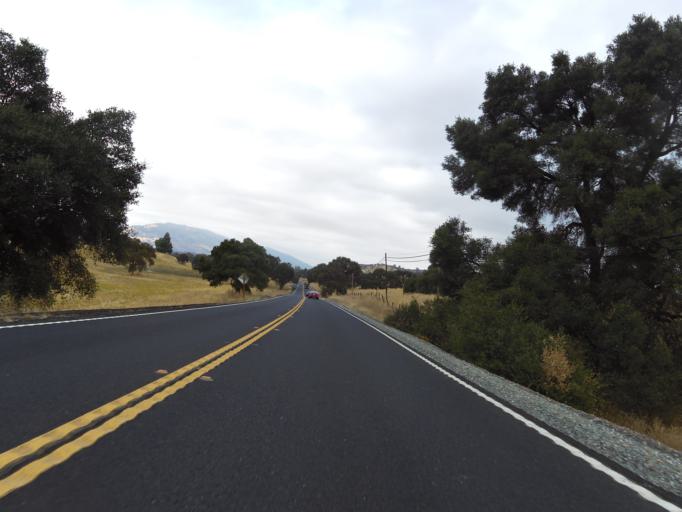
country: US
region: California
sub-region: Calaveras County
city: Angels Camp
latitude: 38.1055
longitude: -120.5942
